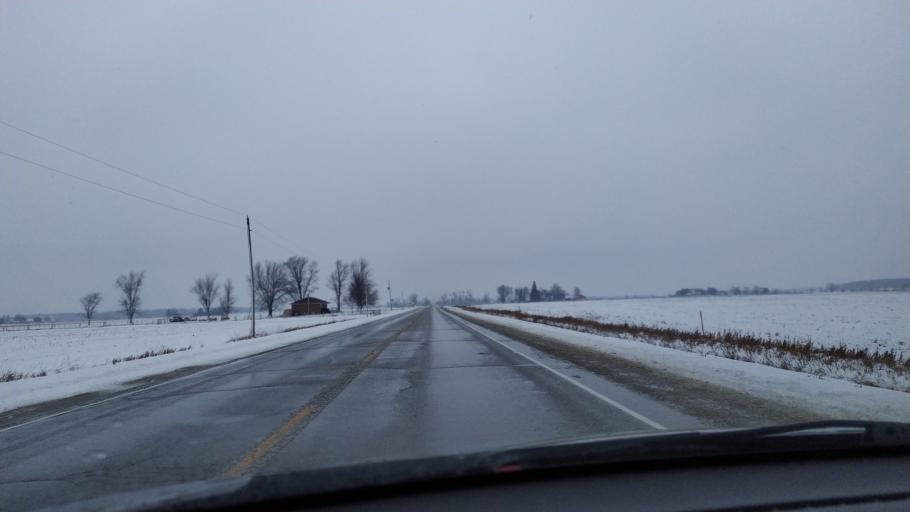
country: CA
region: Ontario
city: Stratford
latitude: 43.5442
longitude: -80.8609
